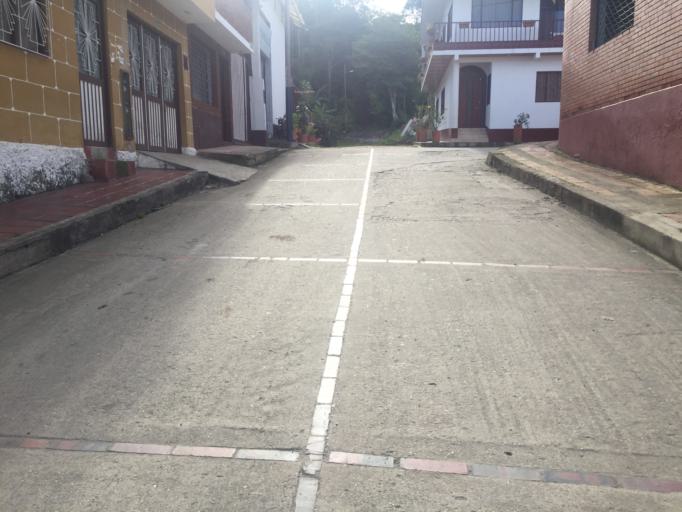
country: CO
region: Cundinamarca
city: Tenza
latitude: 5.0956
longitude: -73.4456
